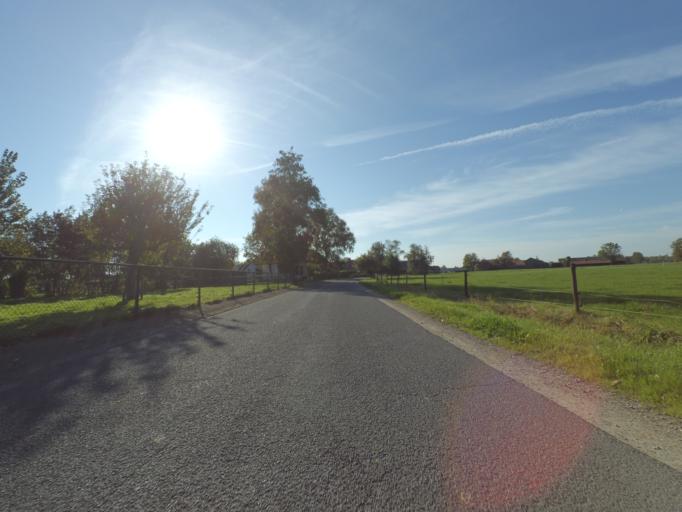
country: NL
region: Gelderland
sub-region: Gemeente Nijkerk
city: Nijkerk
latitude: 52.2039
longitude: 5.4706
